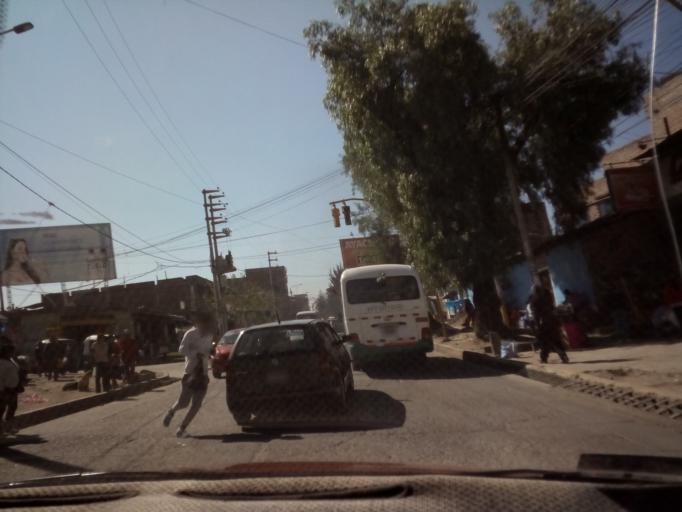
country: PE
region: Ayacucho
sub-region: Provincia de Huamanga
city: Ayacucho
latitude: -13.1665
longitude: -74.2143
